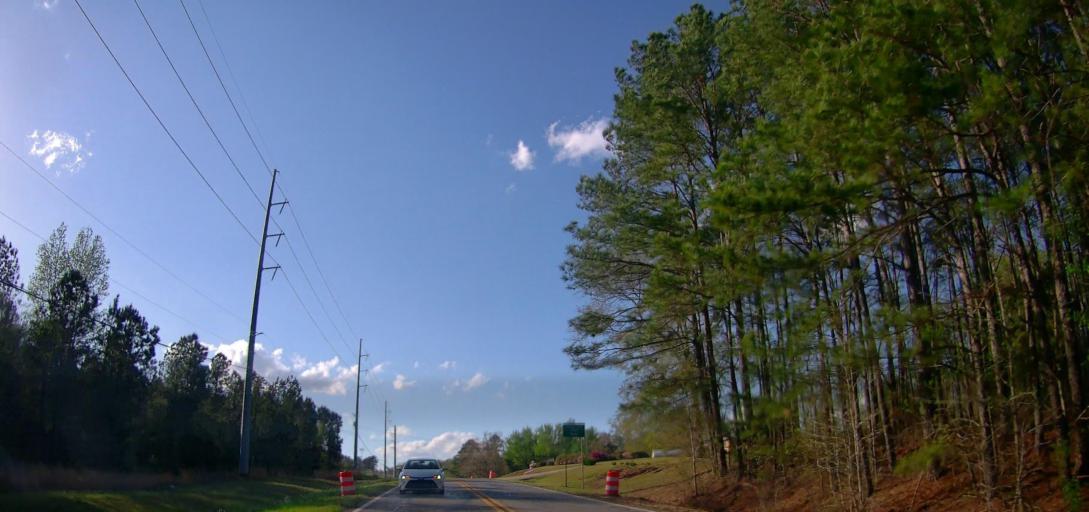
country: US
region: Georgia
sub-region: Baldwin County
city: Milledgeville
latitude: 33.1035
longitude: -83.2754
